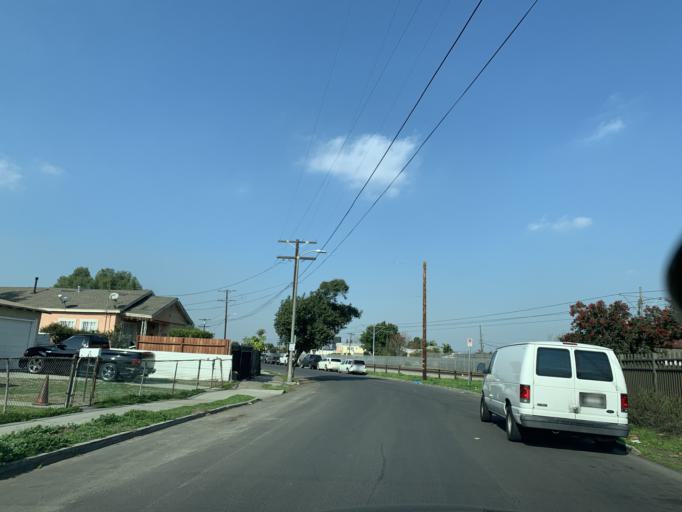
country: US
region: California
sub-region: Los Angeles County
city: Willowbrook
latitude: 33.9321
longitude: -118.2402
